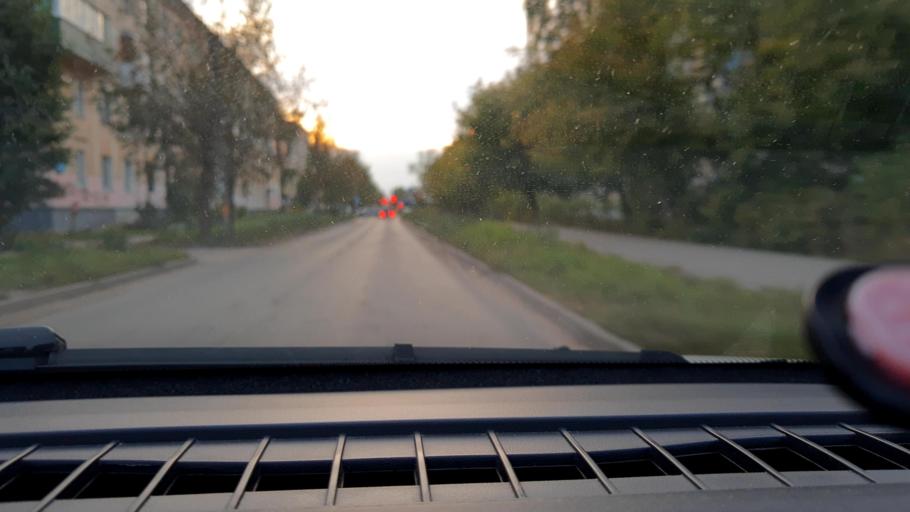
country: RU
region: Nizjnij Novgorod
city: Dzerzhinsk
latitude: 56.2458
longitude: 43.4698
